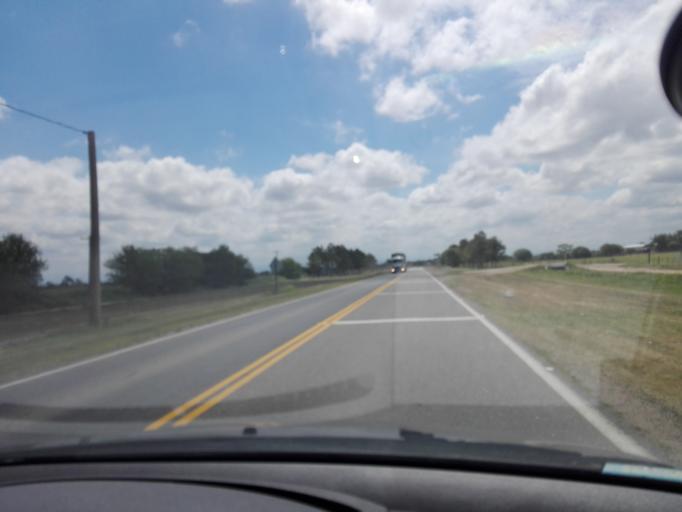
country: AR
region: Cordoba
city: Toledo
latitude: -31.6502
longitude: -64.0929
